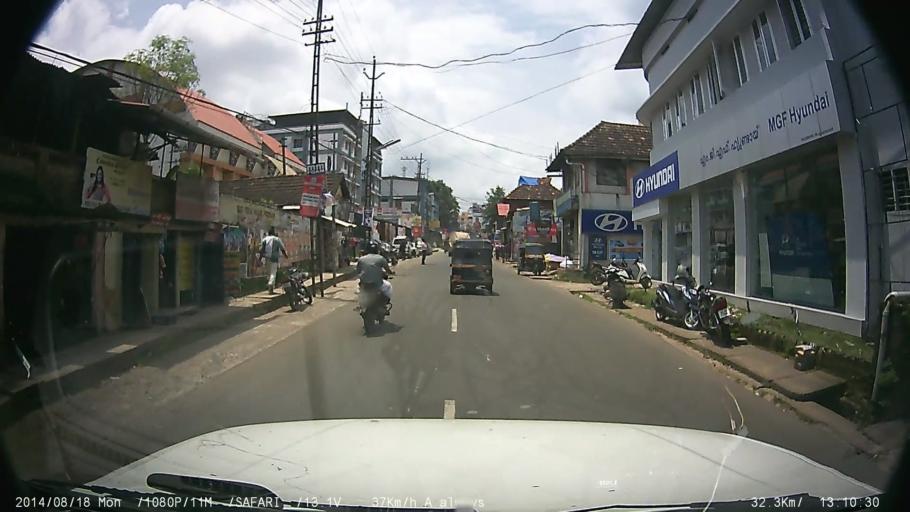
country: IN
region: Kerala
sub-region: Kottayam
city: Kottayam
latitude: 9.5860
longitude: 76.5217
